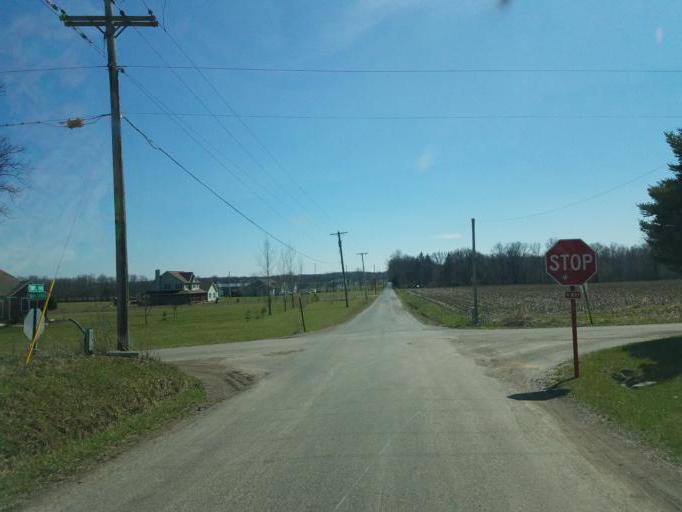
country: US
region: Ohio
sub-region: Ashland County
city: Ashland
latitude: 40.8907
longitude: -82.3585
